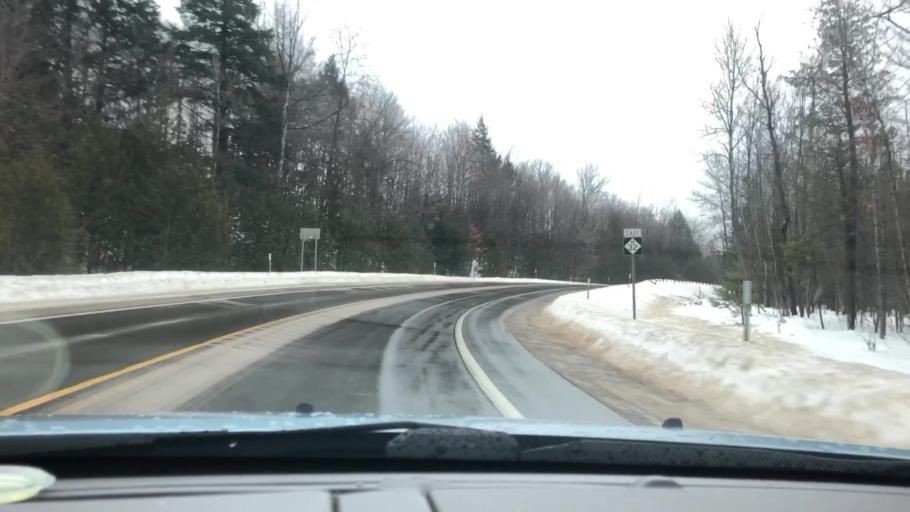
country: US
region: Michigan
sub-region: Charlevoix County
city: East Jordan
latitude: 45.1321
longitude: -85.0817
